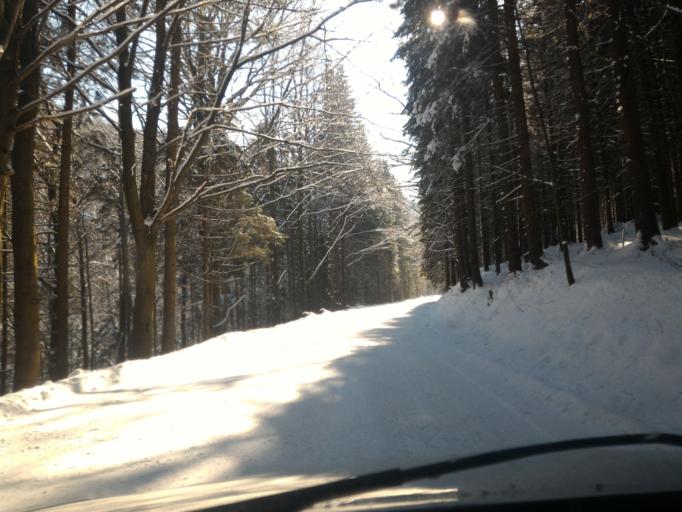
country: CZ
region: Liberecky
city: Nove Mesto pod Smrkem
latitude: 50.8600
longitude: 15.2588
